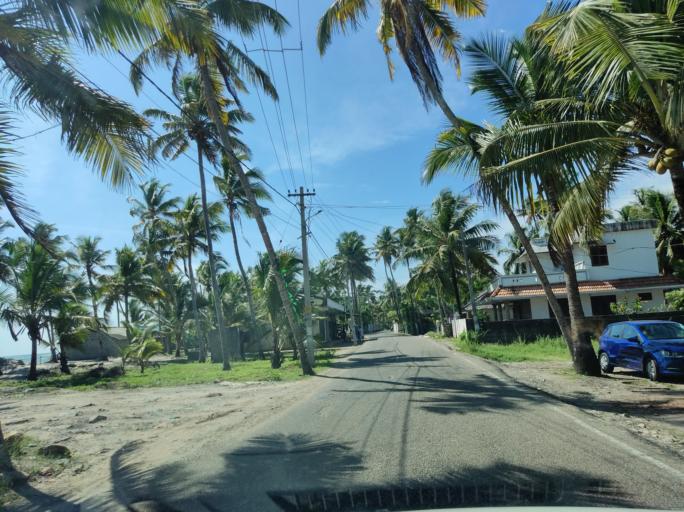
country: IN
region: Kerala
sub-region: Alappuzha
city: Kayankulam
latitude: 9.2418
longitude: 76.4151
